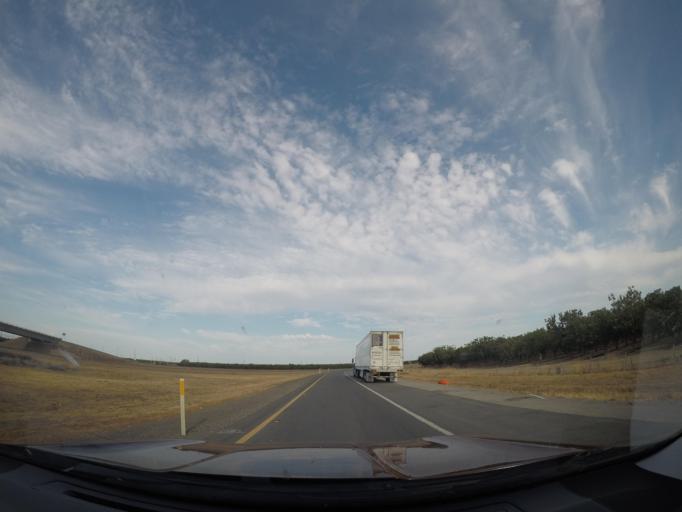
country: US
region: California
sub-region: Colusa County
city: Arbuckle
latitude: 39.0561
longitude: -122.0873
